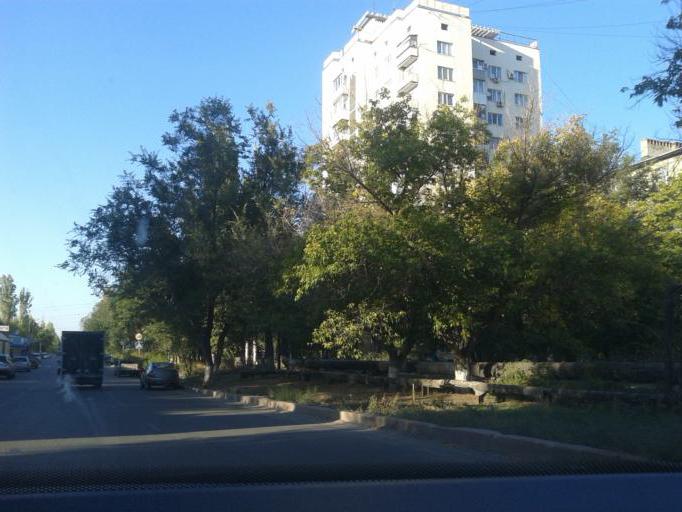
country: RU
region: Volgograd
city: Gorodishche
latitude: 48.7602
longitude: 44.4788
